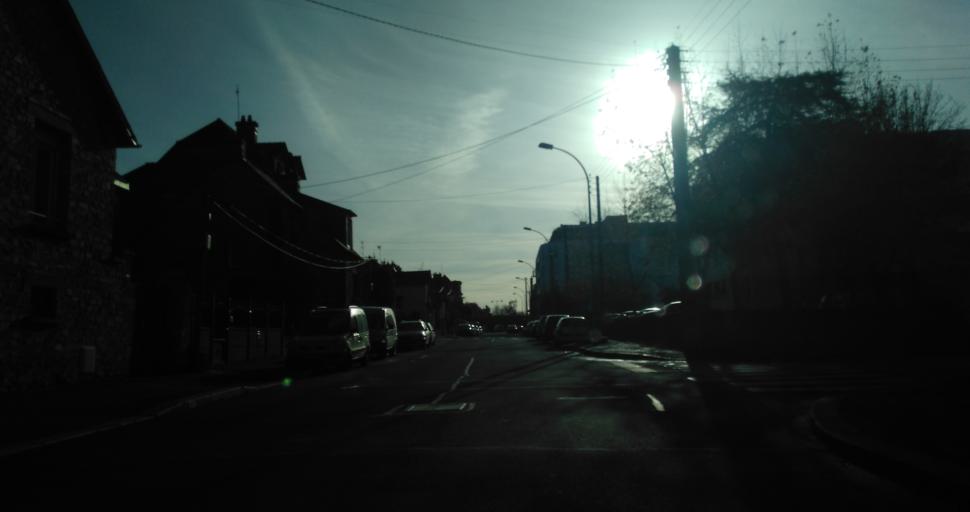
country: FR
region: Brittany
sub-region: Departement d'Ille-et-Vilaine
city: Rennes
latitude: 48.1232
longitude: -1.6647
